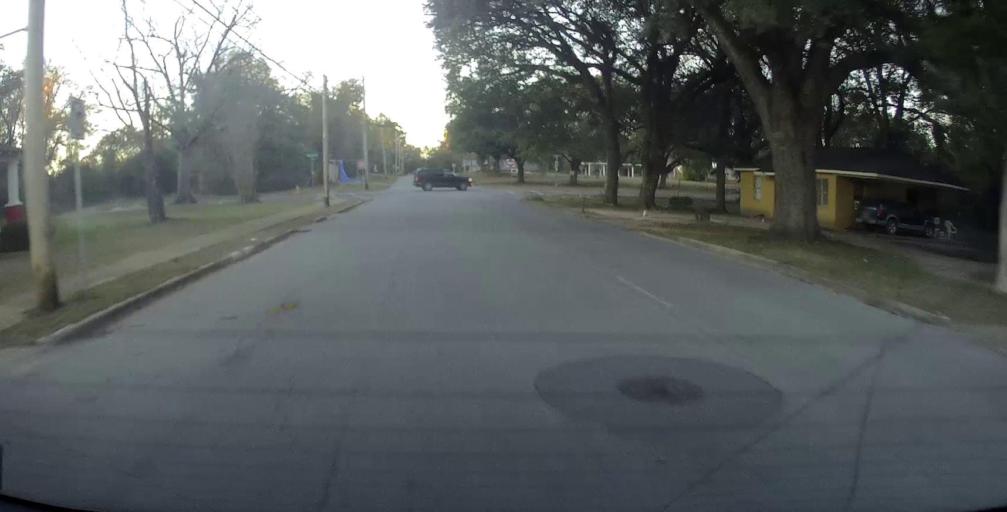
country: US
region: Georgia
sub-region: Dougherty County
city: Albany
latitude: 31.5677
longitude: -84.1619
